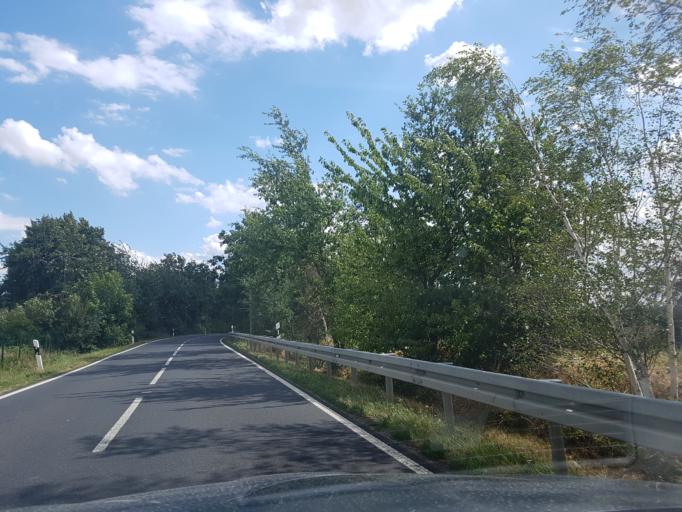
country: DE
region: Saxony
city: Grossenhain
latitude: 51.2610
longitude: 13.5456
